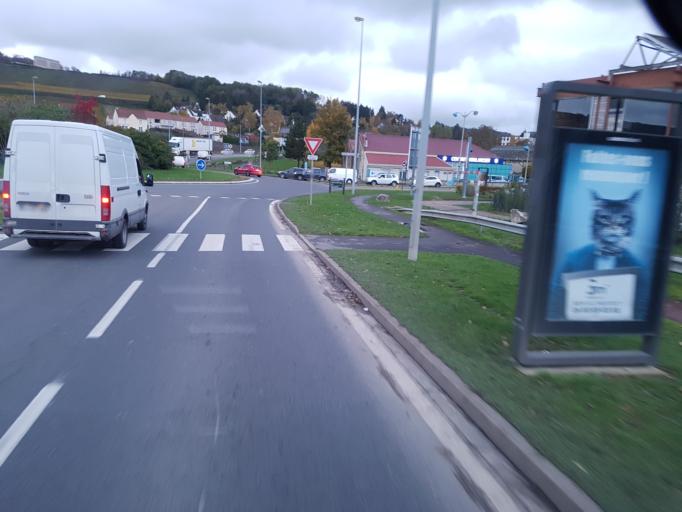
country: FR
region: Picardie
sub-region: Departement de l'Aisne
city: Essomes-sur-Marne
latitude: 49.0358
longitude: 3.3814
